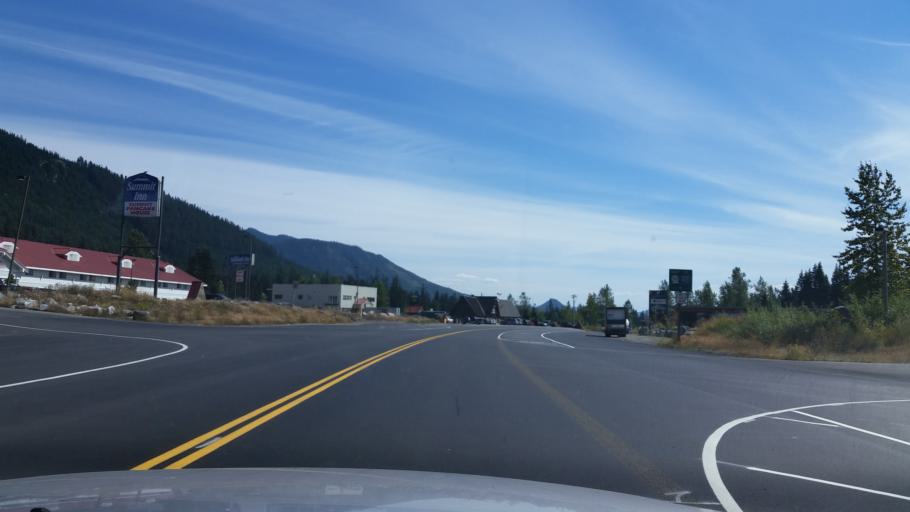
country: US
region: Washington
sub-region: King County
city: Tanner
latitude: 47.4227
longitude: -121.4130
